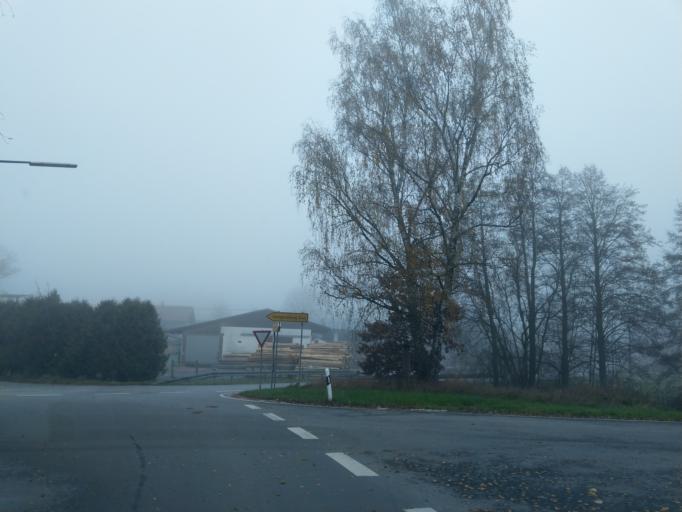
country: DE
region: Bavaria
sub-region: Lower Bavaria
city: Auerbach
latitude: 48.7727
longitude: 13.0919
